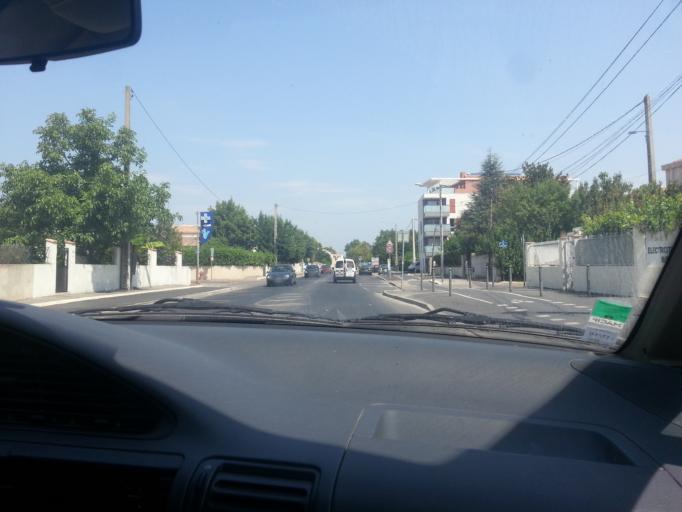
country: FR
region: Languedoc-Roussillon
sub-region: Departement de l'Herault
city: Castelnau-le-Lez
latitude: 43.6142
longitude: 3.8981
